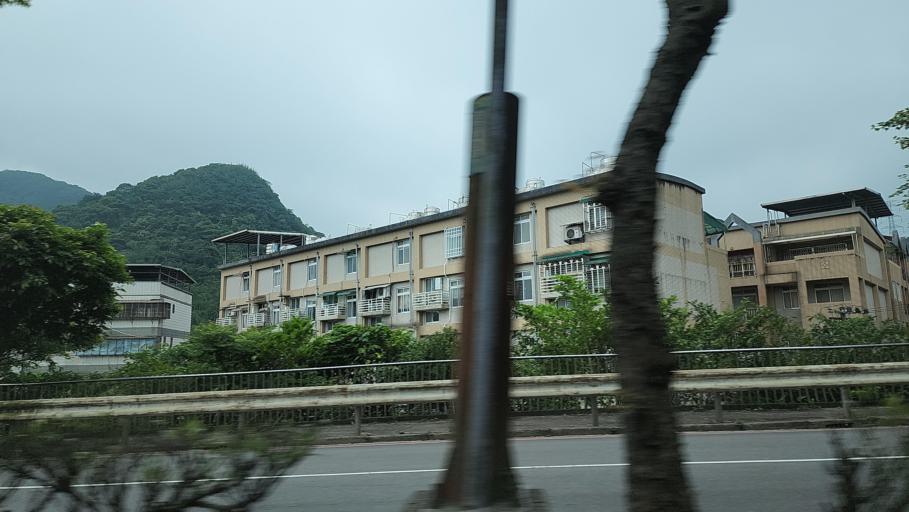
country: TW
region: Taiwan
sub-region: Keelung
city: Keelung
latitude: 25.1592
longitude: 121.6945
